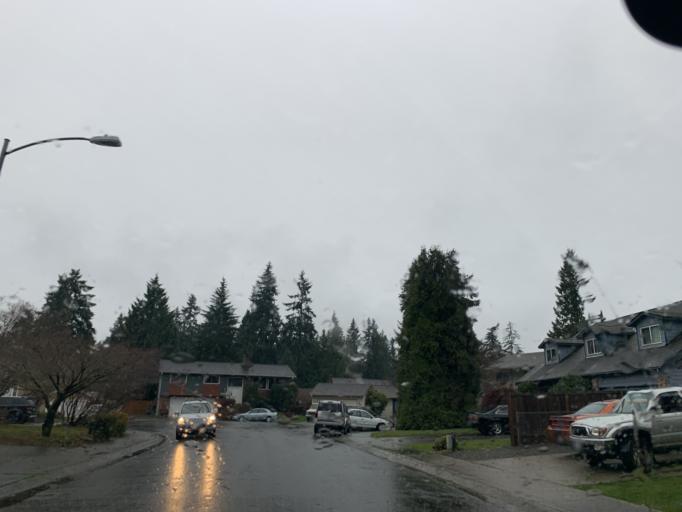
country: US
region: Washington
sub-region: King County
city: Kingsgate
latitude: 47.7381
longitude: -122.1836
